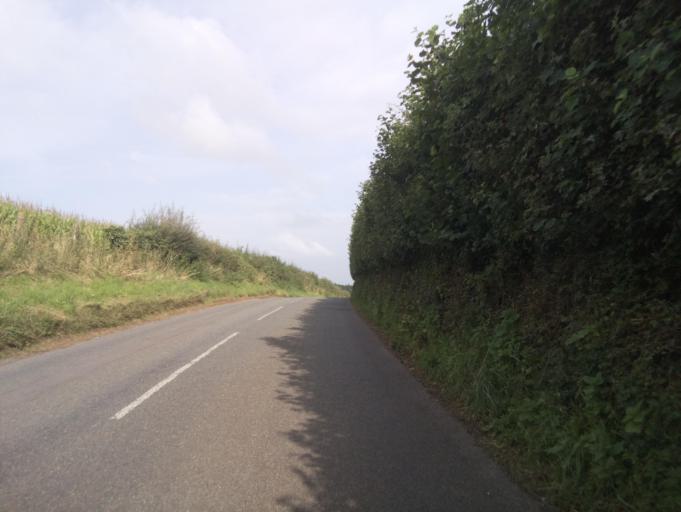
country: GB
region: England
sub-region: Bath and North East Somerset
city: East Harptree
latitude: 51.2932
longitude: -2.5971
